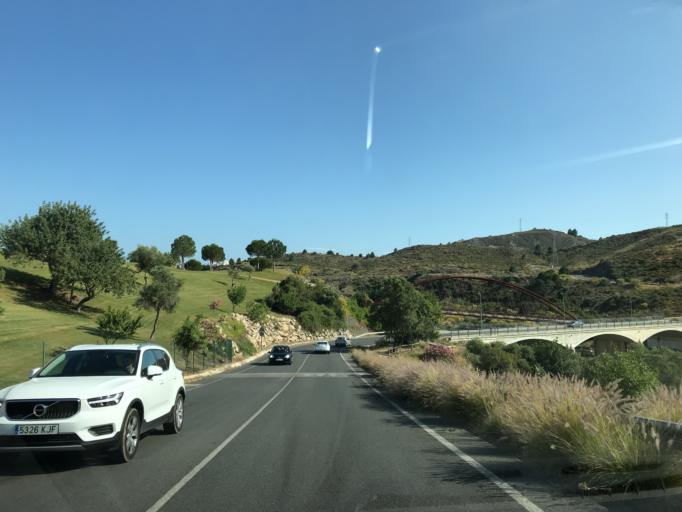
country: ES
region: Andalusia
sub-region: Provincia de Malaga
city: Benahavis
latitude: 36.5032
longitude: -5.0241
